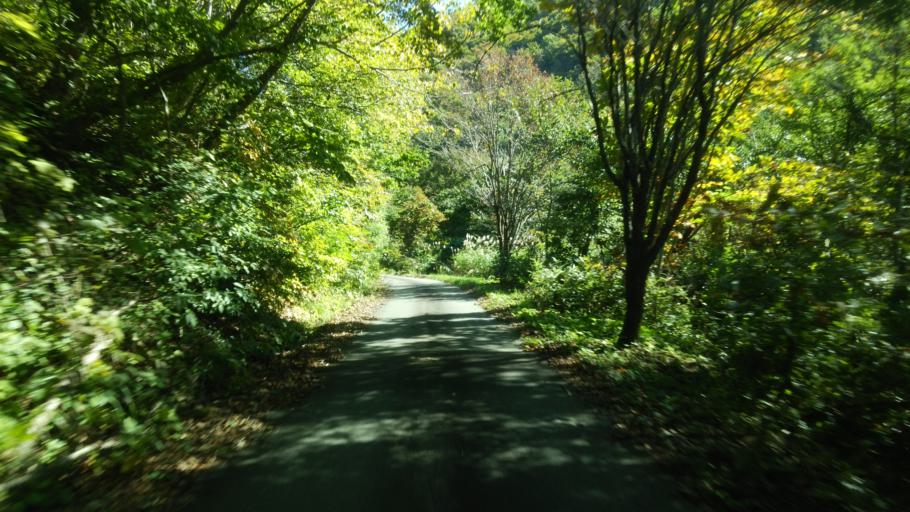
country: JP
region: Fukushima
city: Kitakata
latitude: 37.6199
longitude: 139.9830
